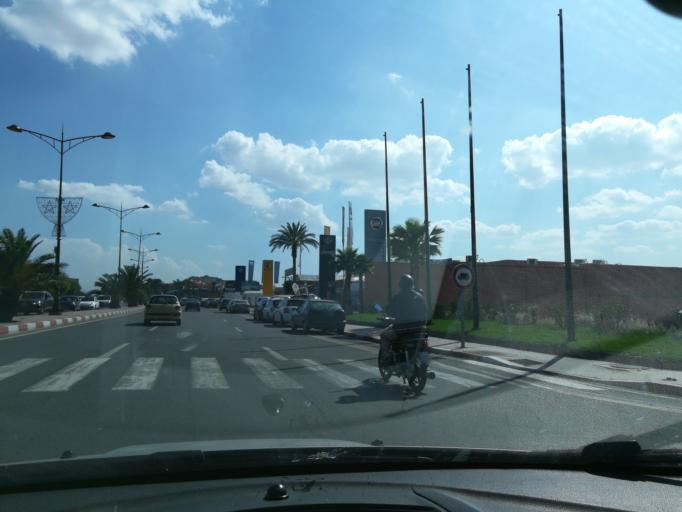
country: MA
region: Marrakech-Tensift-Al Haouz
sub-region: Marrakech
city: Marrakesh
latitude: 31.6581
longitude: -8.0174
